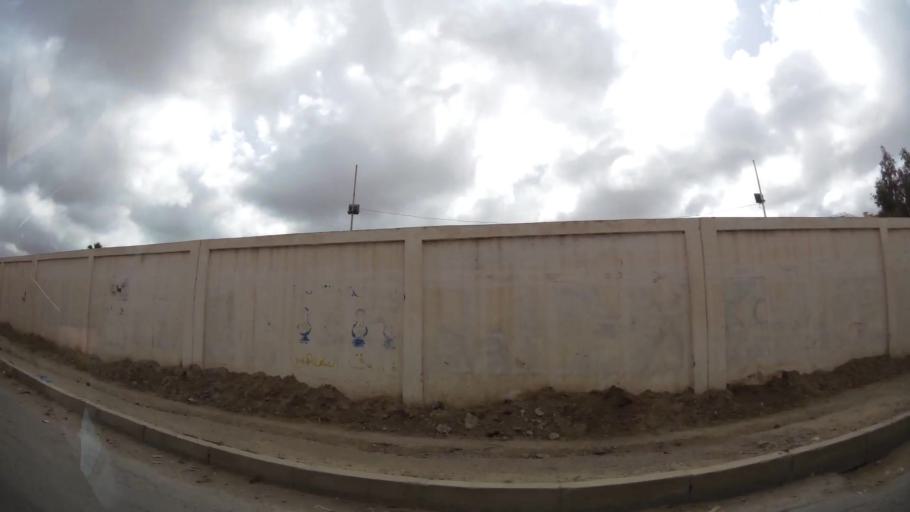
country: MA
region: Oriental
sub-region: Nador
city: Nador
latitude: 35.1657
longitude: -2.9418
